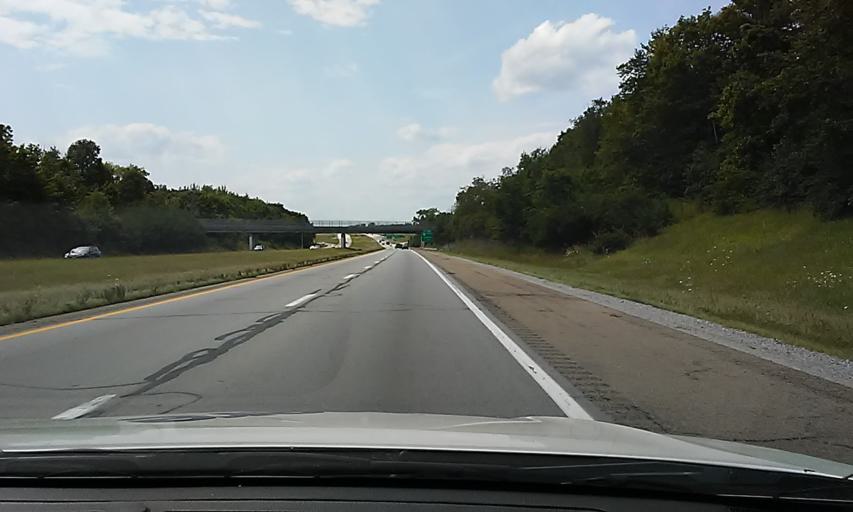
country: US
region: Ohio
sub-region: Clark County
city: Springfield
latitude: 39.8953
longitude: -83.8420
